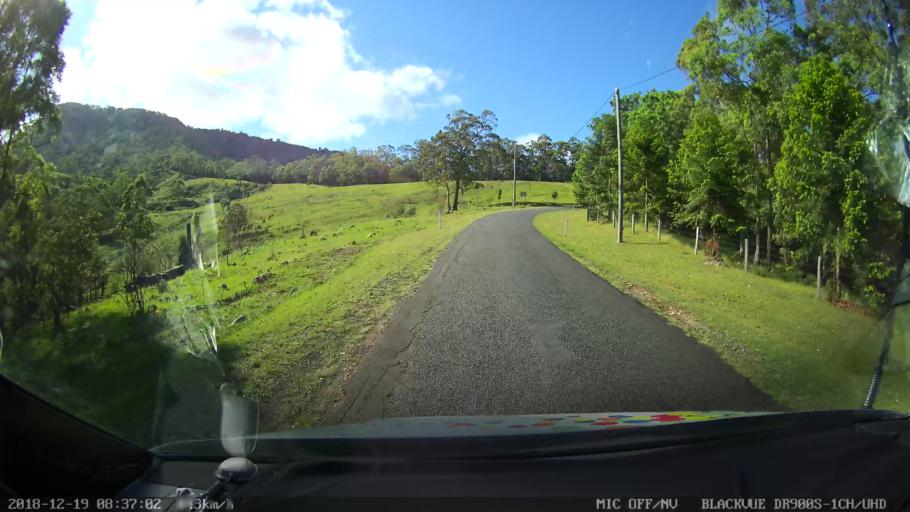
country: AU
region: New South Wales
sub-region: Kyogle
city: Kyogle
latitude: -28.3297
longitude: 152.9733
